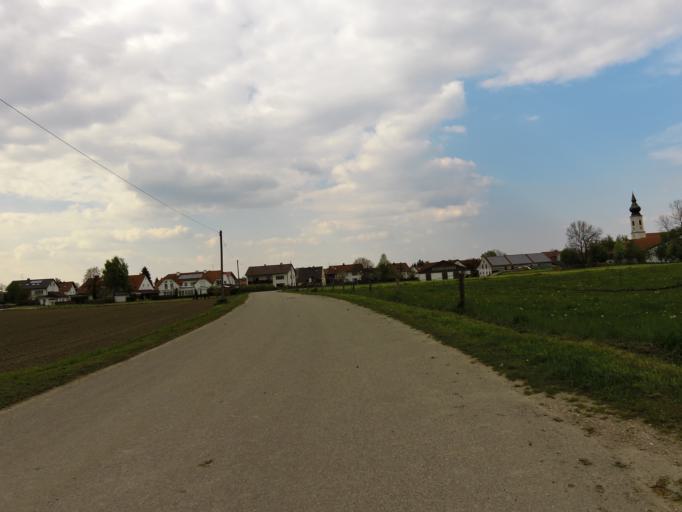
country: DE
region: Bavaria
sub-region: Upper Bavaria
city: Langenpreising
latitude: 48.4216
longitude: 11.9694
